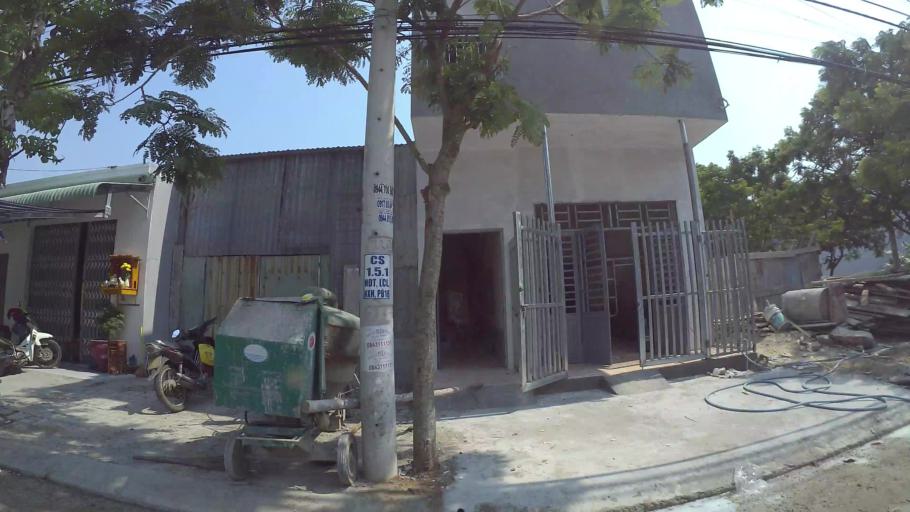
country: VN
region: Da Nang
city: Cam Le
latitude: 16.0100
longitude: 108.2019
